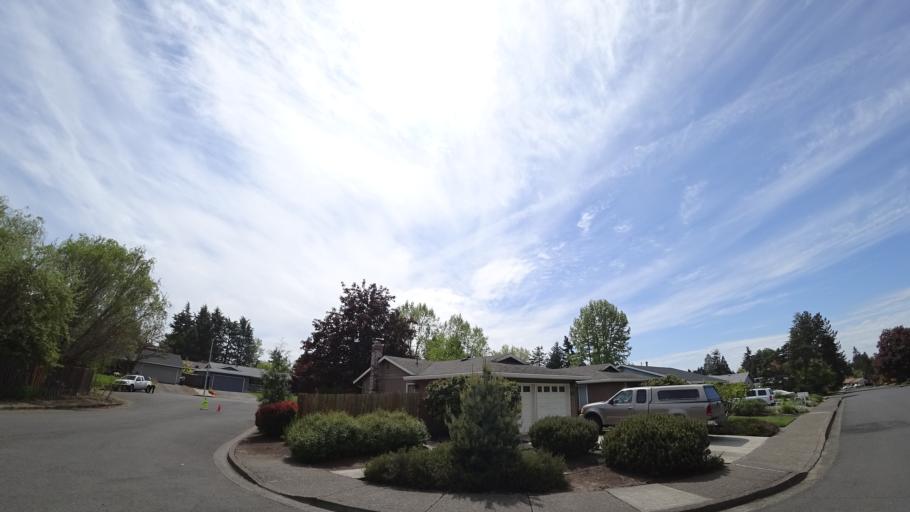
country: US
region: Oregon
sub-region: Washington County
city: Aloha
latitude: 45.4815
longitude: -122.8880
